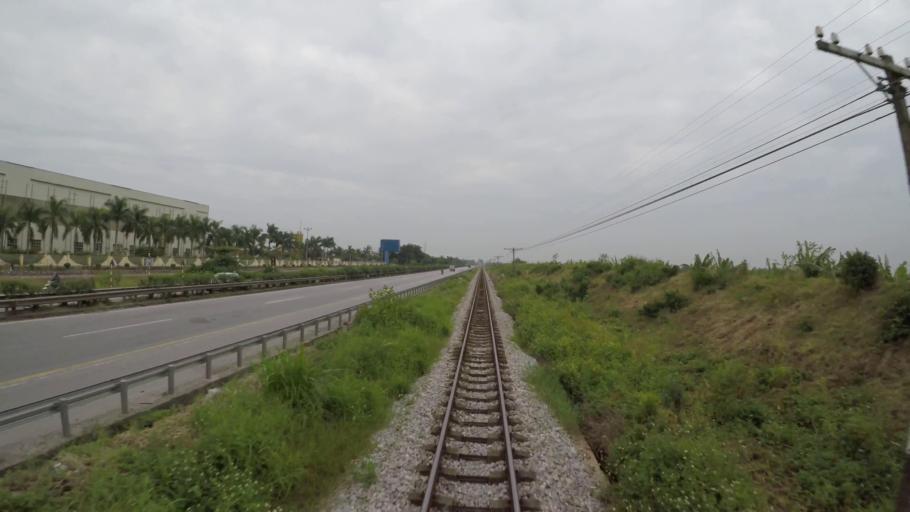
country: VN
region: Hai Duong
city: Nam Sach
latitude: 20.9761
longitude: 106.4004
